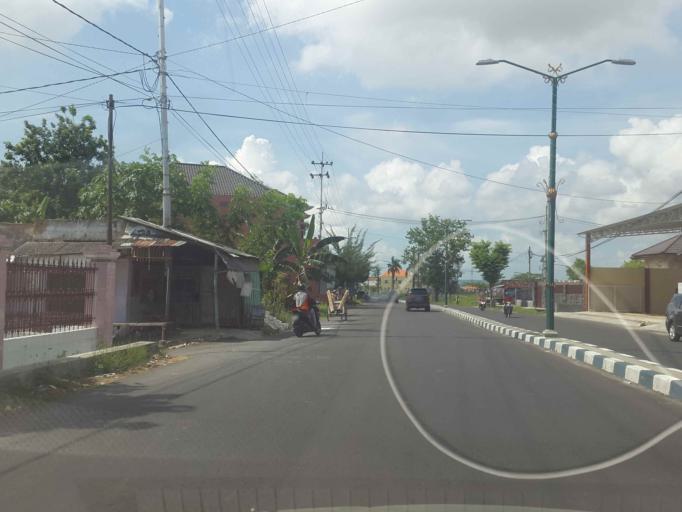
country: ID
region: East Java
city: Sumenep
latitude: -7.0296
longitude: 113.8528
